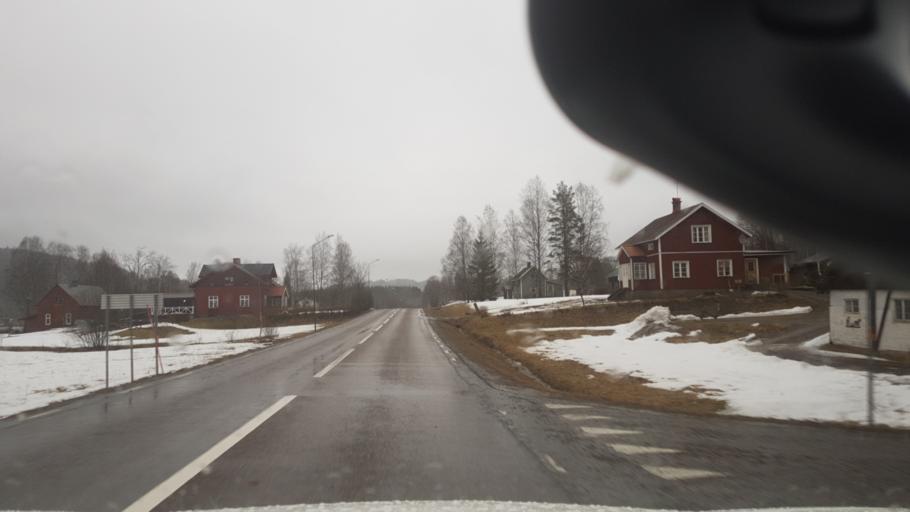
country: SE
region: Vaermland
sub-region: Arjangs Kommun
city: Arjaeng
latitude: 59.5876
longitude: 12.1290
